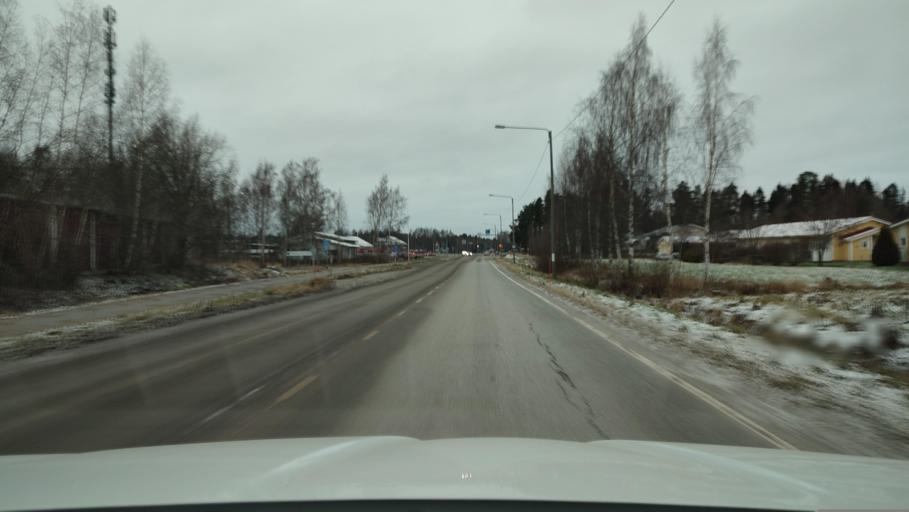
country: FI
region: Ostrobothnia
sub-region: Vaasa
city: Smedsby
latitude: 63.1185
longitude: 21.7120
